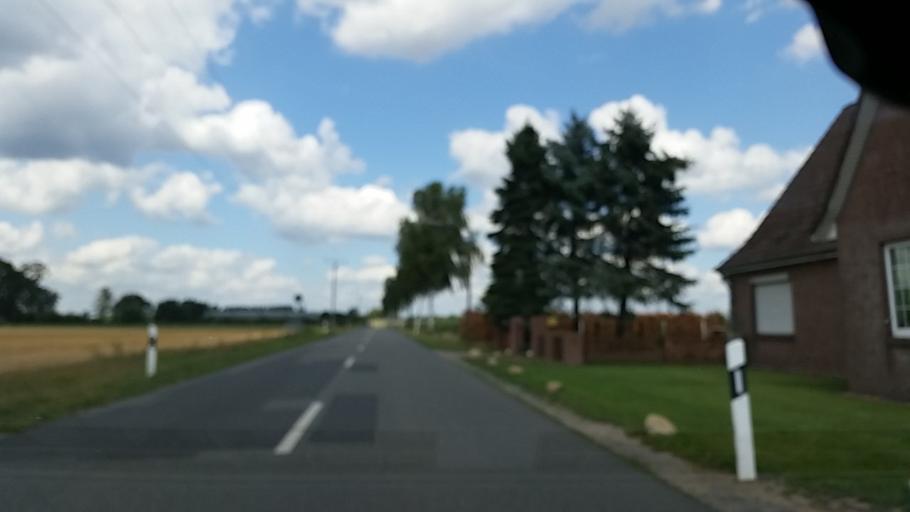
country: DE
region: Lower Saxony
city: Sprakensehl
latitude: 52.7381
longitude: 10.5135
